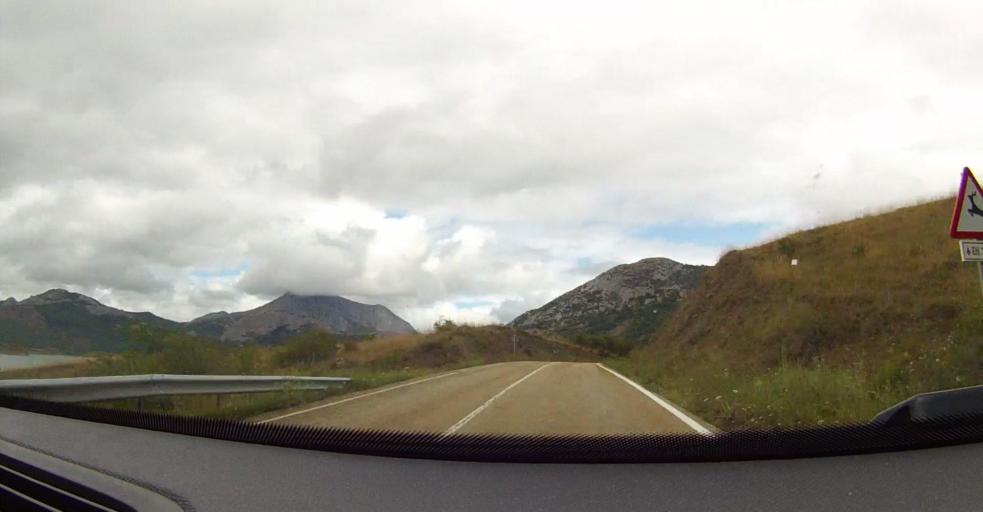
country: ES
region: Castille and Leon
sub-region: Provincia de Leon
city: Puebla de Lillo
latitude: 42.9394
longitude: -5.2691
